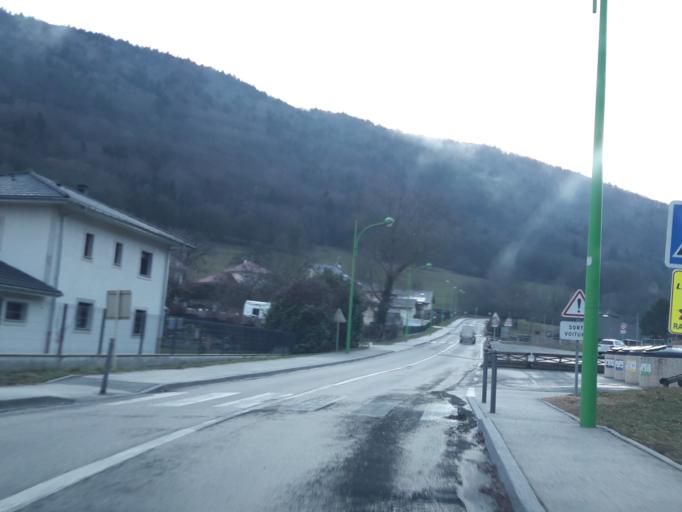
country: FR
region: Rhone-Alpes
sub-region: Departement de la Haute-Savoie
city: Monnetier-Mornex
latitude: 46.1589
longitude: 6.2141
